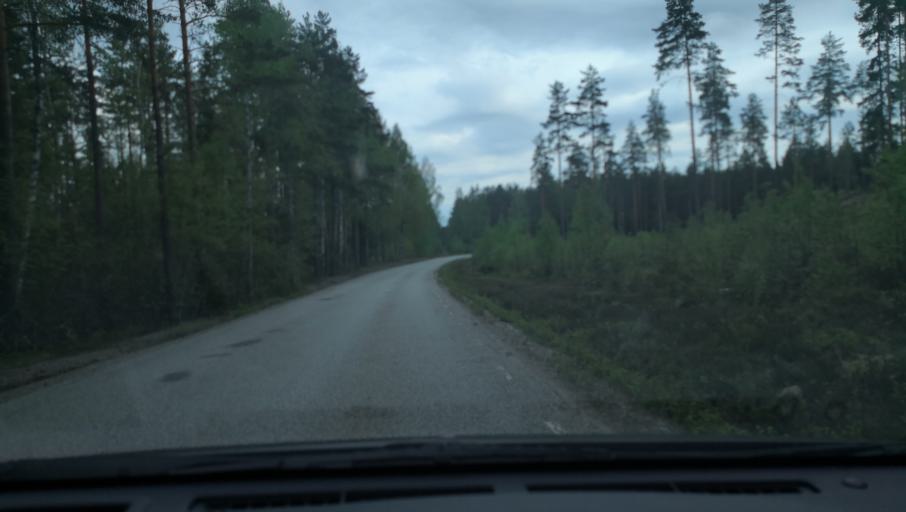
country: SE
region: Vaestmanland
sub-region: Skinnskattebergs Kommun
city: Skinnskatteberg
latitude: 59.8134
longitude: 15.5573
